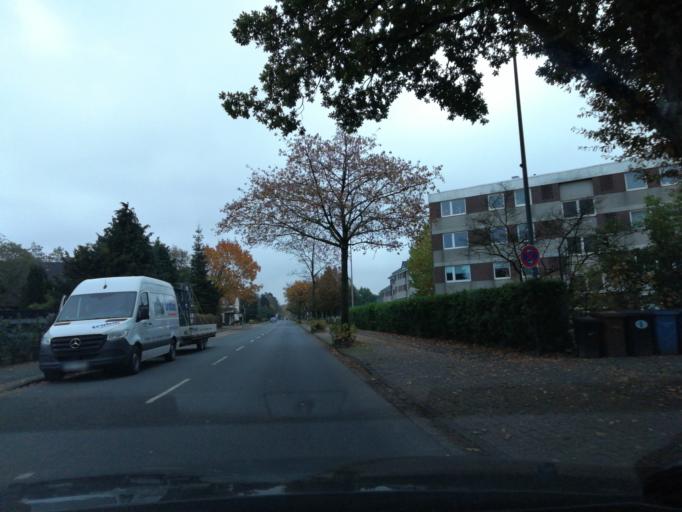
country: DE
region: Lower Saxony
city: Schortens
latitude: 53.5443
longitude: 7.9392
